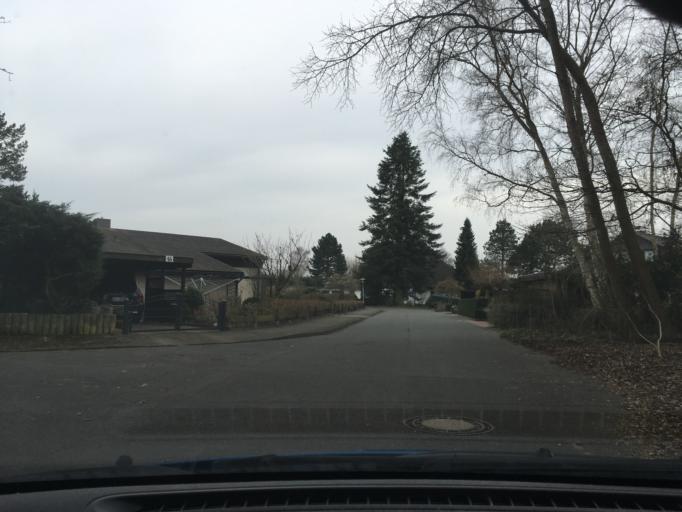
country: DE
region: Lower Saxony
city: Tespe
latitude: 53.3917
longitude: 10.4181
